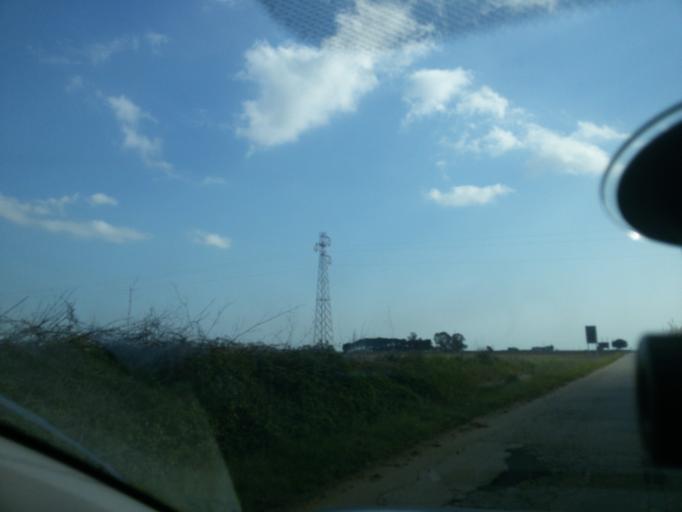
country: IT
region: Apulia
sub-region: Provincia di Brindisi
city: Mesagne
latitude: 40.6498
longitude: 17.8155
